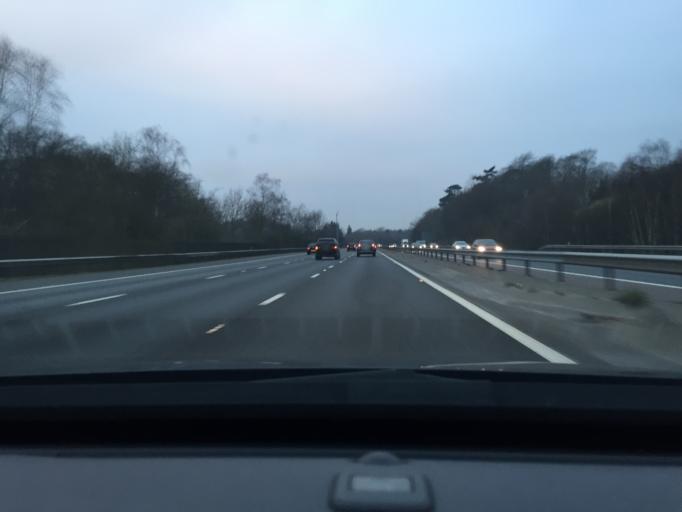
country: GB
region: England
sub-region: Hampshire
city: Botley
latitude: 50.8794
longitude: -1.2770
